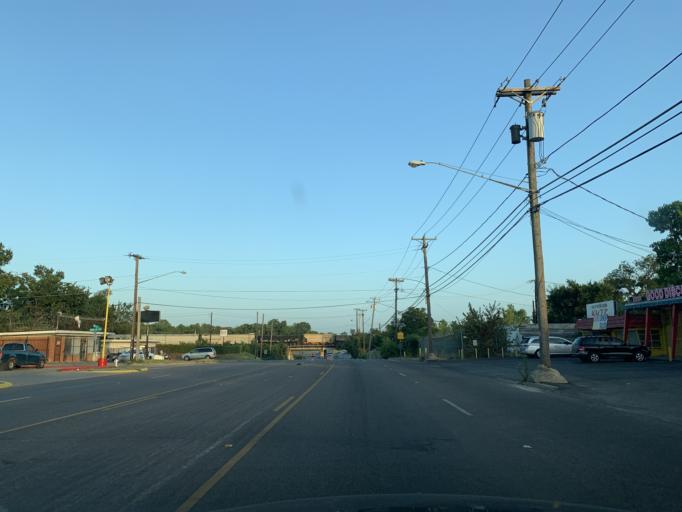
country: US
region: Texas
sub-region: Dallas County
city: Dallas
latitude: 32.7595
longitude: -96.7429
